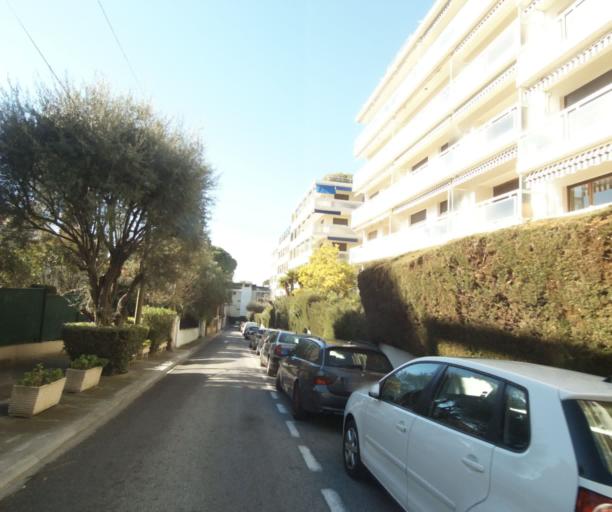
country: FR
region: Provence-Alpes-Cote d'Azur
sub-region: Departement des Alpes-Maritimes
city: Antibes
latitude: 43.5648
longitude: 7.1189
